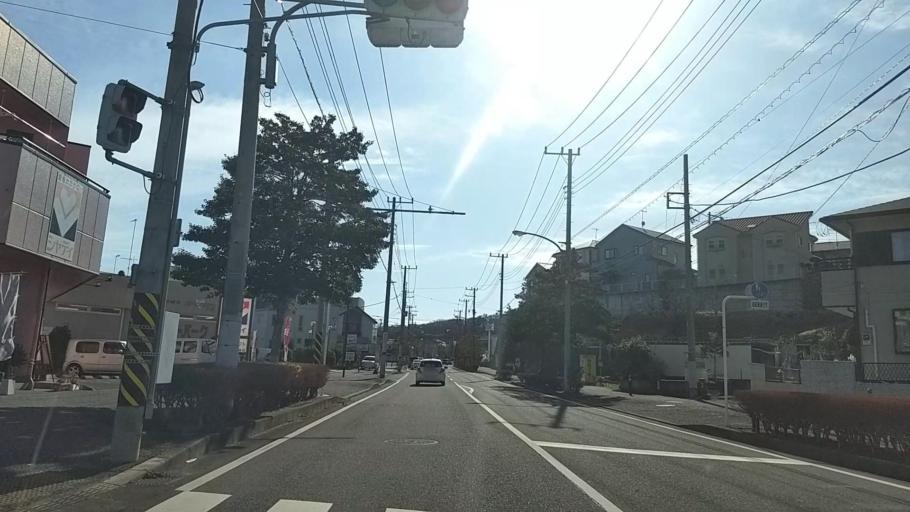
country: JP
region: Kanagawa
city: Hadano
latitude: 35.3636
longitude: 139.2267
